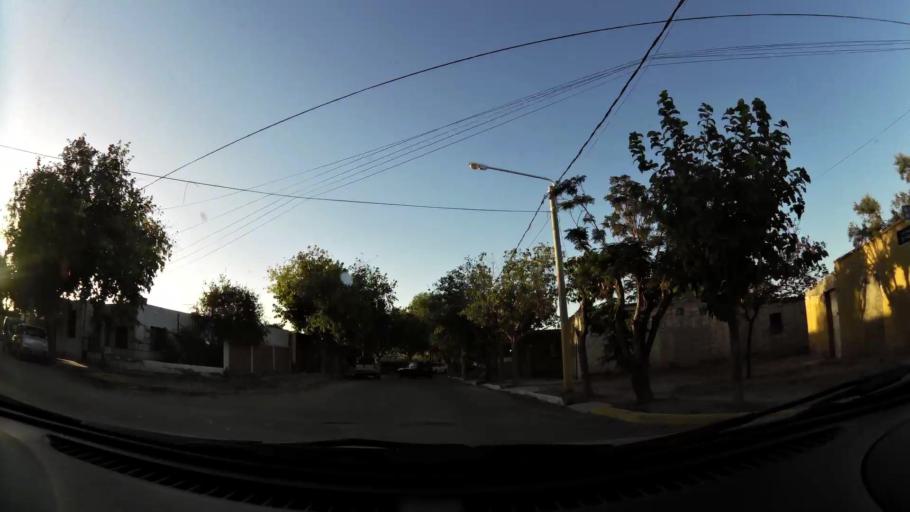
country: AR
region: San Juan
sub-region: Departamento de Santa Lucia
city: Santa Lucia
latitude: -31.5258
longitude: -68.5071
